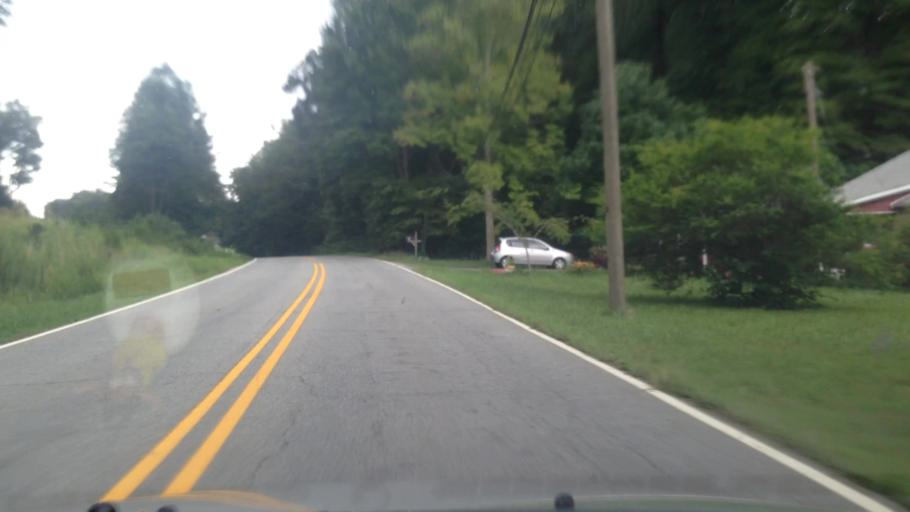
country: US
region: North Carolina
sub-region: Forsyth County
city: Walkertown
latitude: 36.2000
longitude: -80.1662
